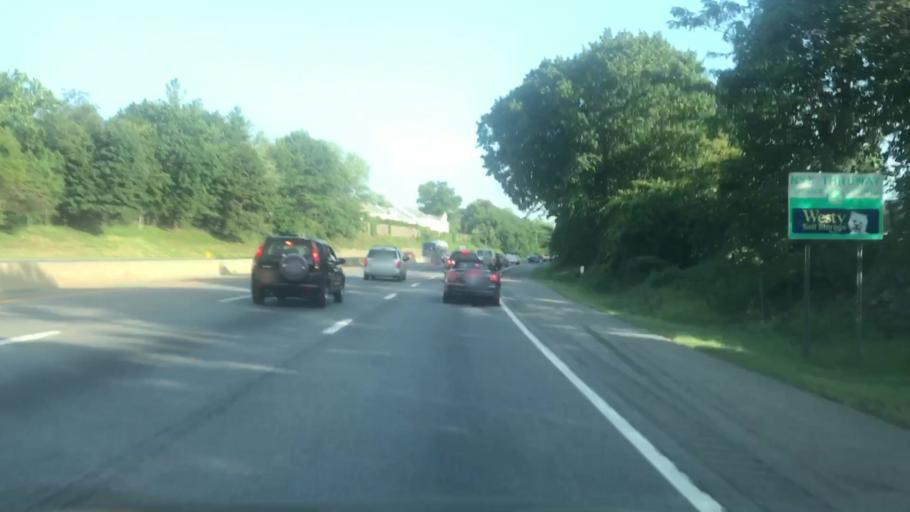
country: US
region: New York
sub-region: Westchester County
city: Rye Brook
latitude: 41.0003
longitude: -73.6850
